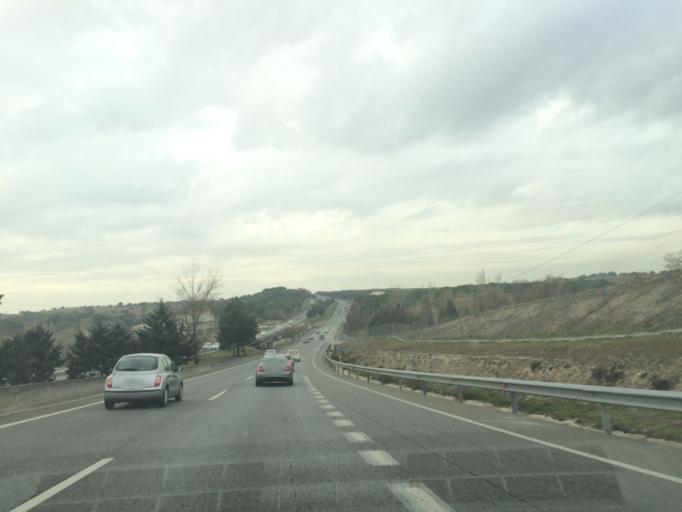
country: ES
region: Madrid
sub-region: Provincia de Madrid
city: Arroyomolinos
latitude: 40.2988
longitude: -3.9383
